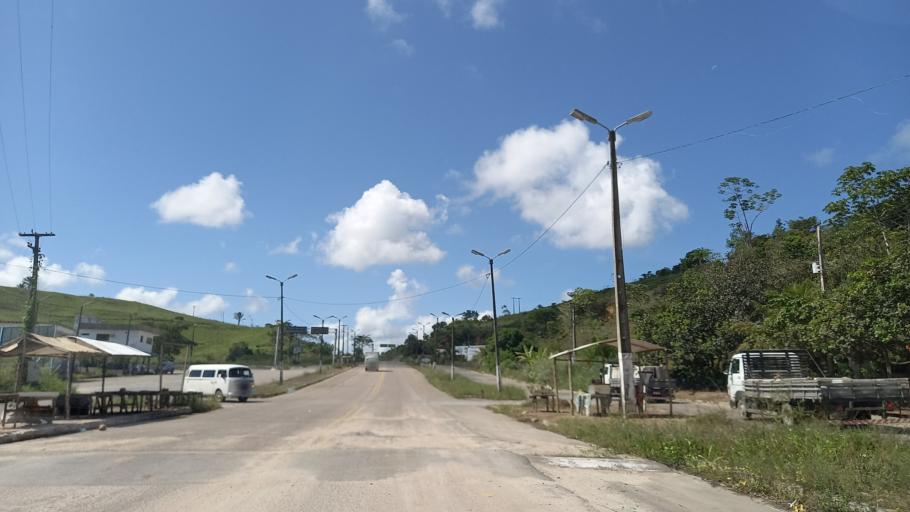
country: BR
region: Pernambuco
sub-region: Barreiros
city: Barreiros
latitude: -8.7914
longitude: -35.1859
